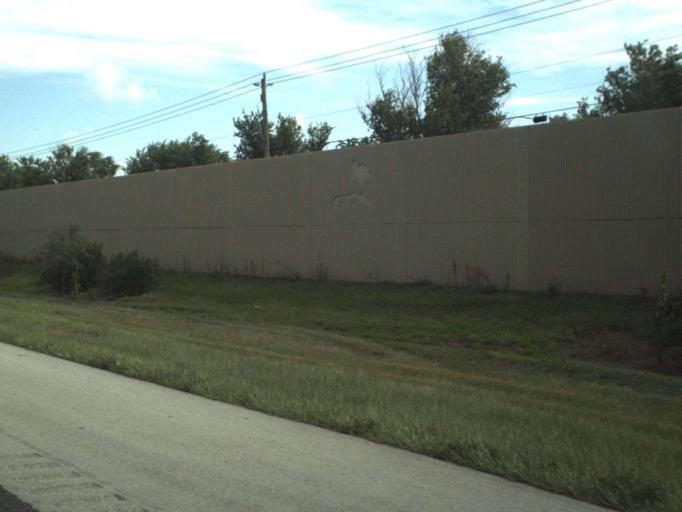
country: US
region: Florida
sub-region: Saint Lucie County
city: Lakewood Park
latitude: 27.5439
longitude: -80.4686
